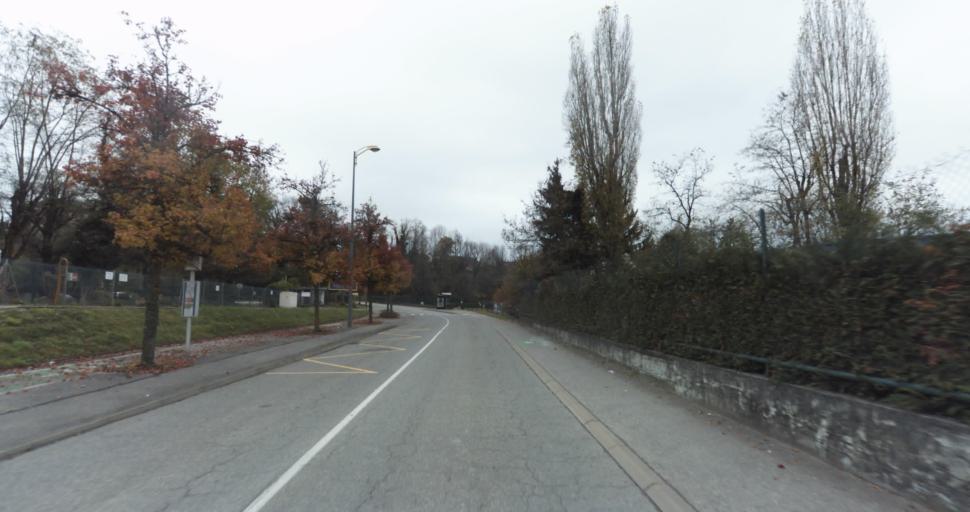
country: FR
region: Rhone-Alpes
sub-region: Departement de la Haute-Savoie
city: Cran-Gevrier
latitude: 45.9118
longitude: 6.1081
